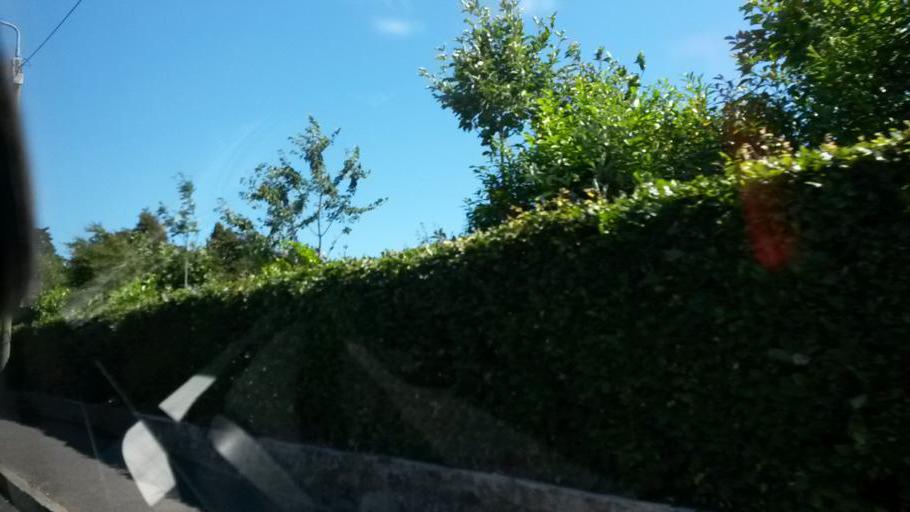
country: IE
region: Leinster
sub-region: Dublin City
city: Finglas
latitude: 53.4306
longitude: -6.3009
